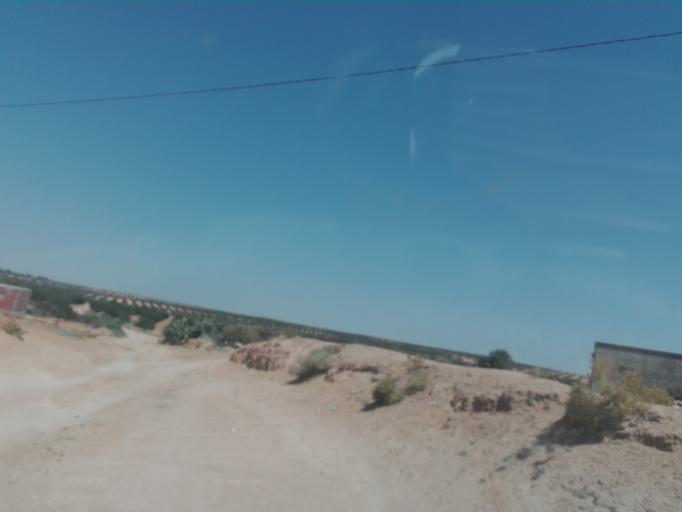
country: TN
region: Safaqis
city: Bi'r `Ali Bin Khalifah
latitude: 34.6470
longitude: 10.2582
